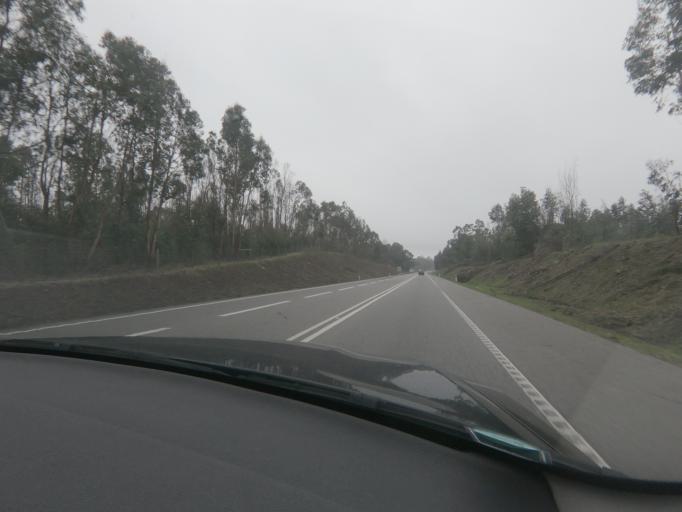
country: PT
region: Viseu
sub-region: Concelho de Tondela
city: Tondela
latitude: 40.5558
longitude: -8.0520
